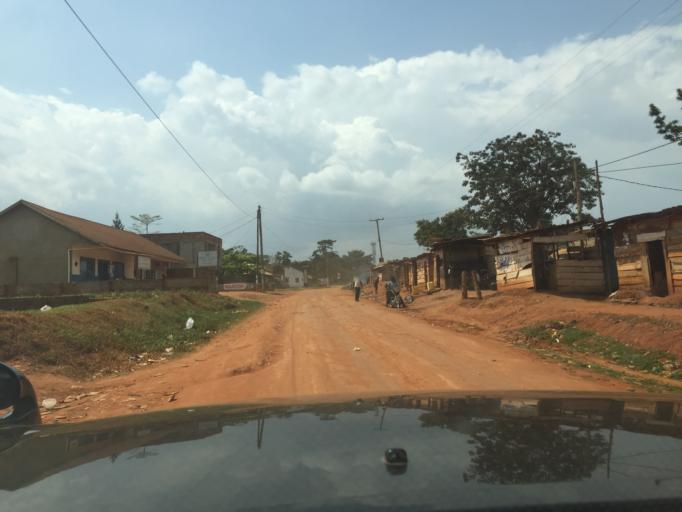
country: UG
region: Central Region
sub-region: Wakiso District
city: Kireka
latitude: 0.4005
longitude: 32.6209
